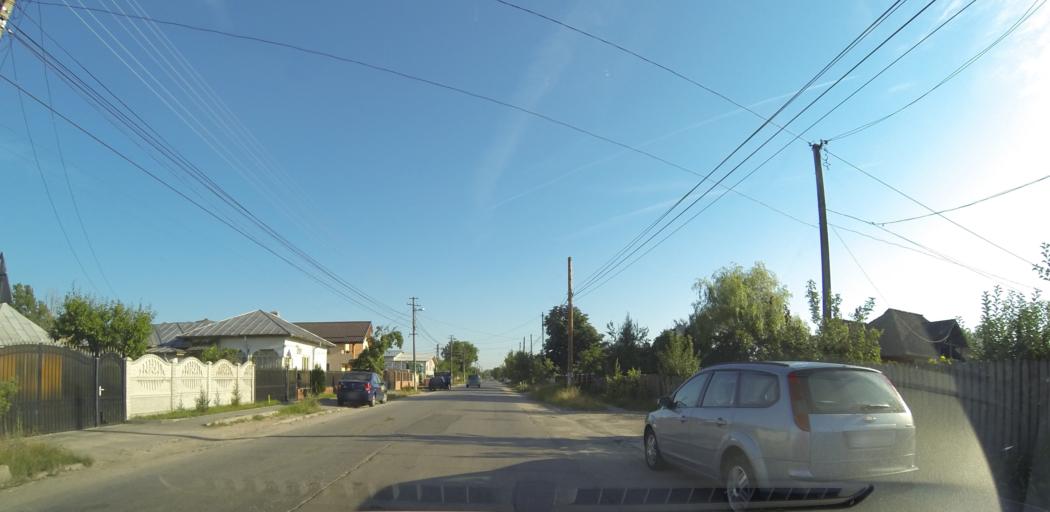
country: RO
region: Valcea
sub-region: Comuna Balcesti
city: Balcesti
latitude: 44.6228
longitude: 23.9421
